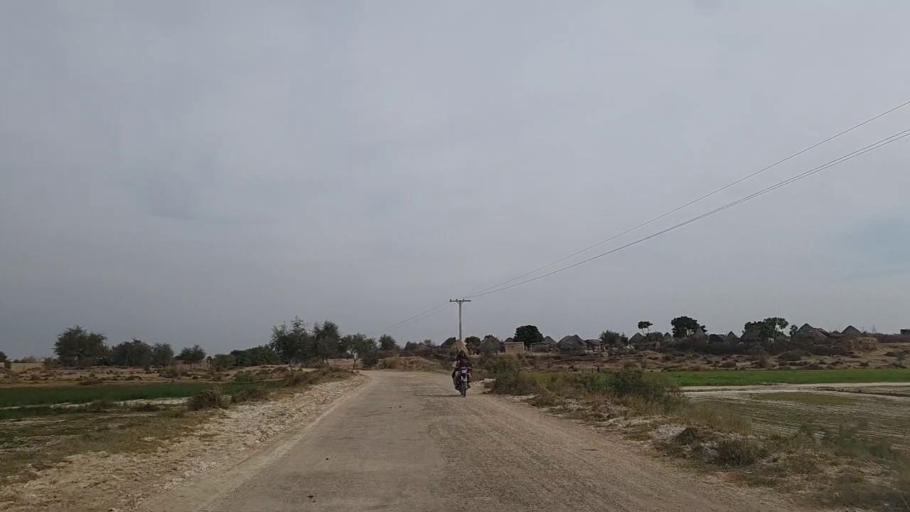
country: PK
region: Sindh
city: Jam Sahib
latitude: 26.4000
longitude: 68.5196
